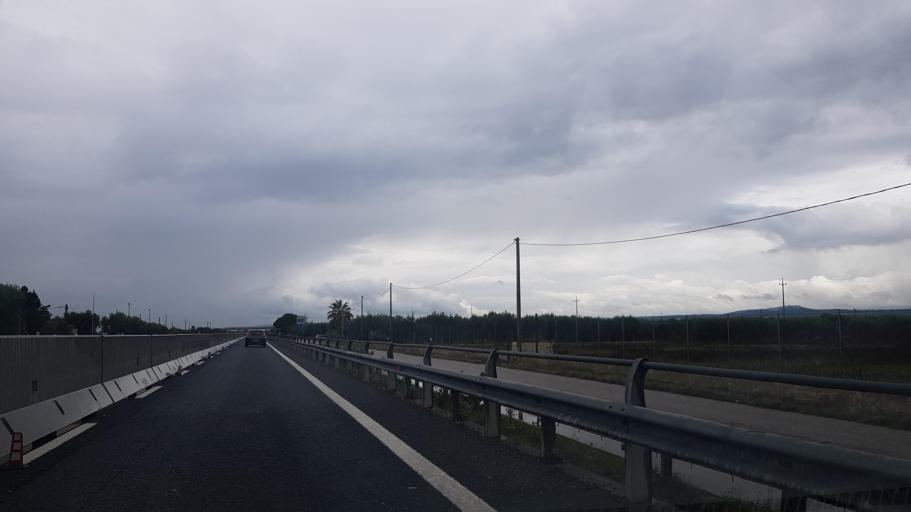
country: IT
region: Apulia
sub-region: Provincia di Taranto
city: Massafra
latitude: 40.5282
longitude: 17.1234
